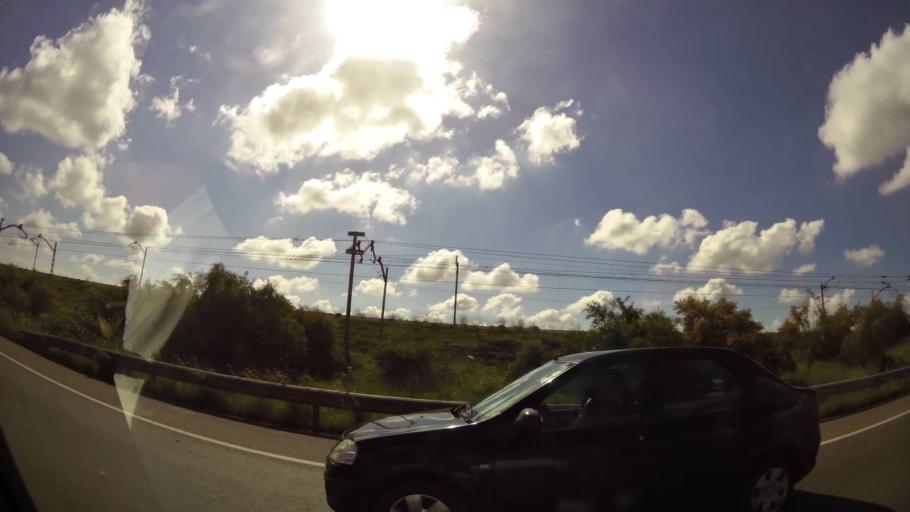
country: MA
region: Chaouia-Ouardigha
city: Nouaseur
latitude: 33.4142
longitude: -7.6265
